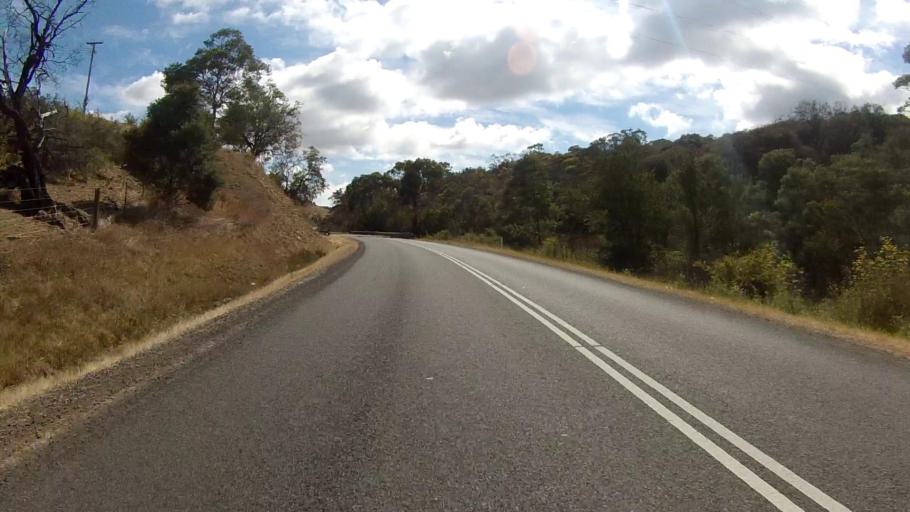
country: AU
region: Tasmania
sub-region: Brighton
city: Old Beach
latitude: -42.7452
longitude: 147.2821
